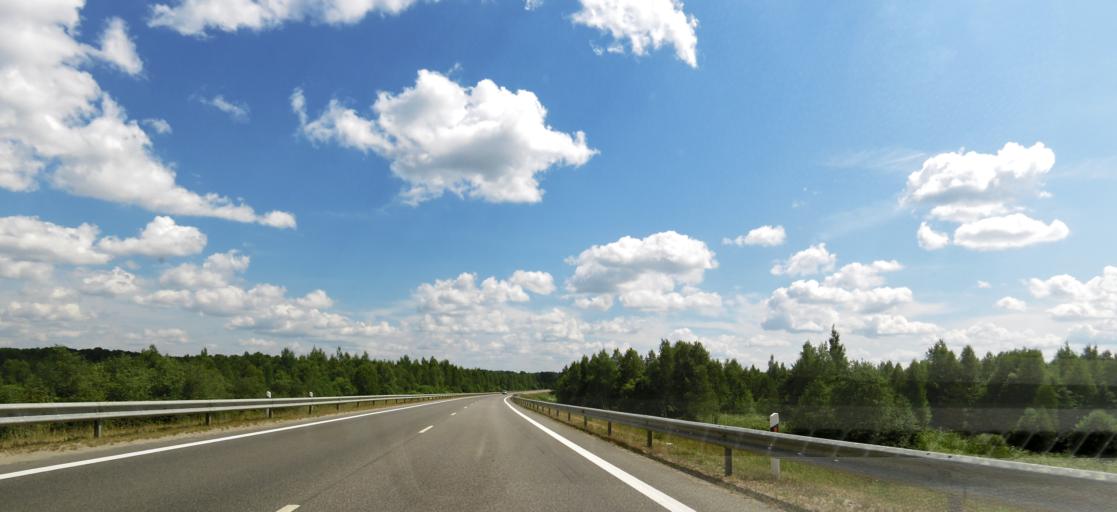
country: LT
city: Skaidiskes
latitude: 54.5618
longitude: 25.6548
